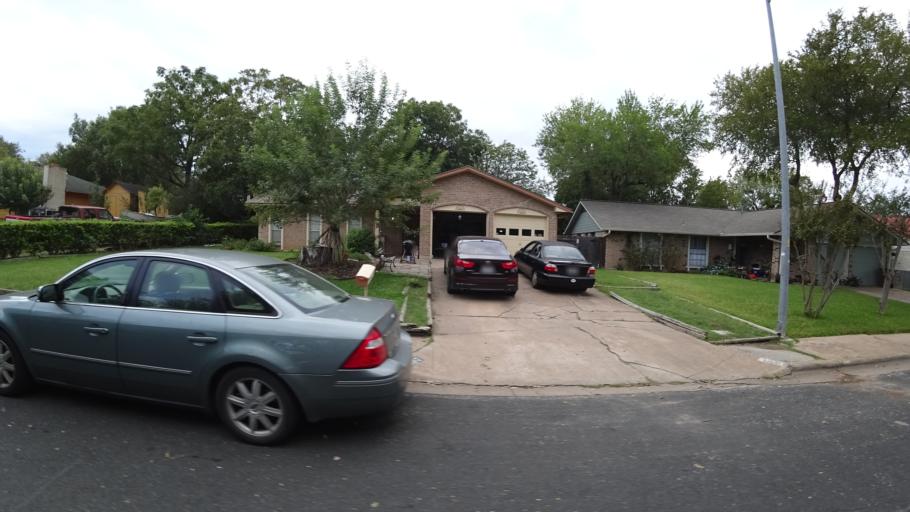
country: US
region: Texas
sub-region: Travis County
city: Rollingwood
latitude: 30.2141
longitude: -97.7904
